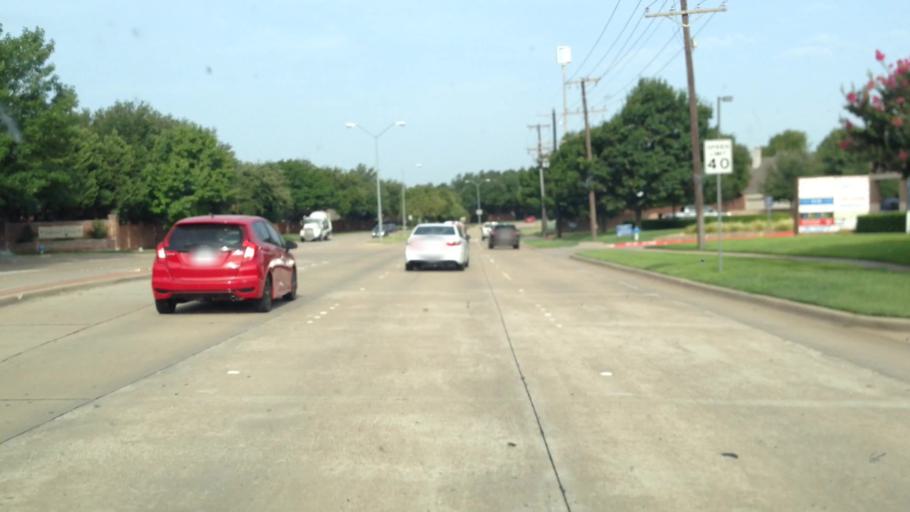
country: US
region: Texas
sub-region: Denton County
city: The Colony
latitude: 33.0453
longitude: -96.8403
